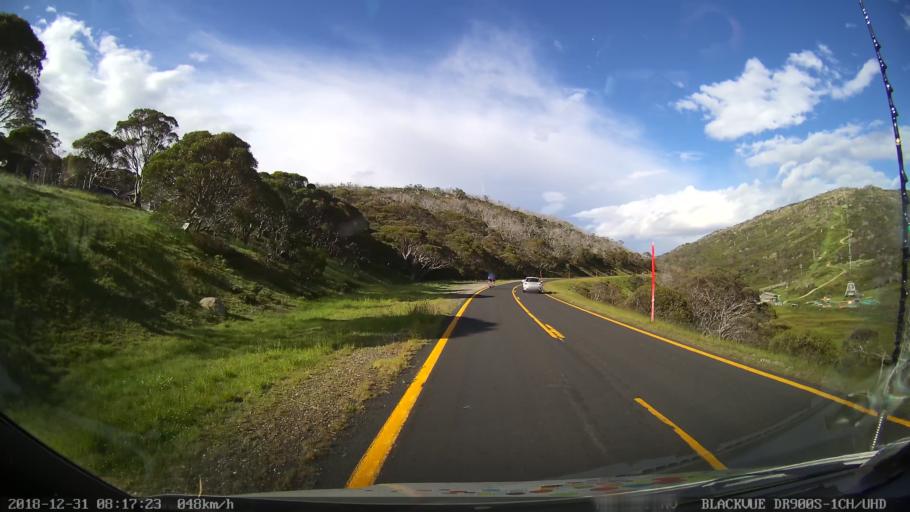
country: AU
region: New South Wales
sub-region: Snowy River
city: Jindabyne
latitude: -36.4103
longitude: 148.4050
